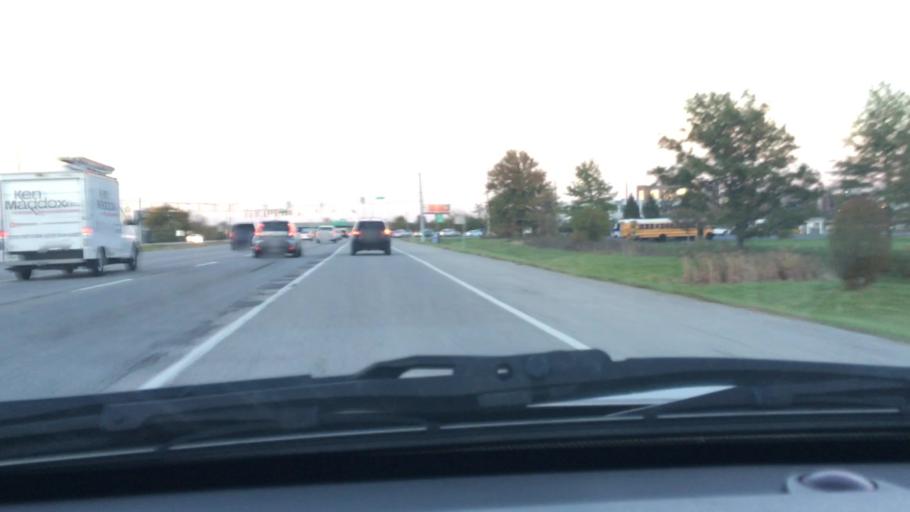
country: US
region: Indiana
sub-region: Marion County
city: Lawrence
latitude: 39.8895
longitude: -86.0597
